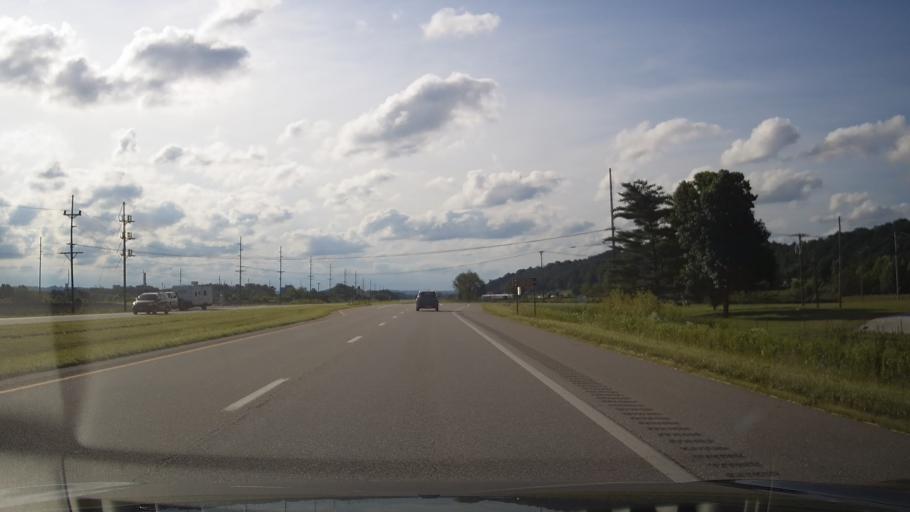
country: US
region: Kentucky
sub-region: Greenup County
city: Greenup
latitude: 38.5913
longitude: -82.8067
